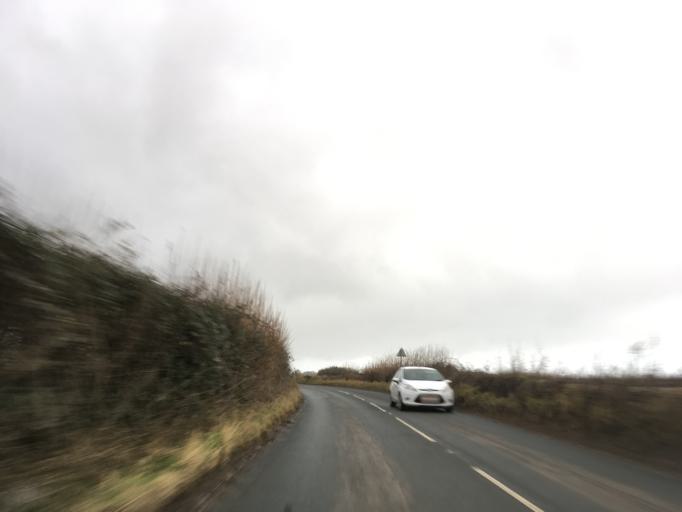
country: GB
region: England
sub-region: Gloucestershire
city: Nailsworth
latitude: 51.6839
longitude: -2.2543
